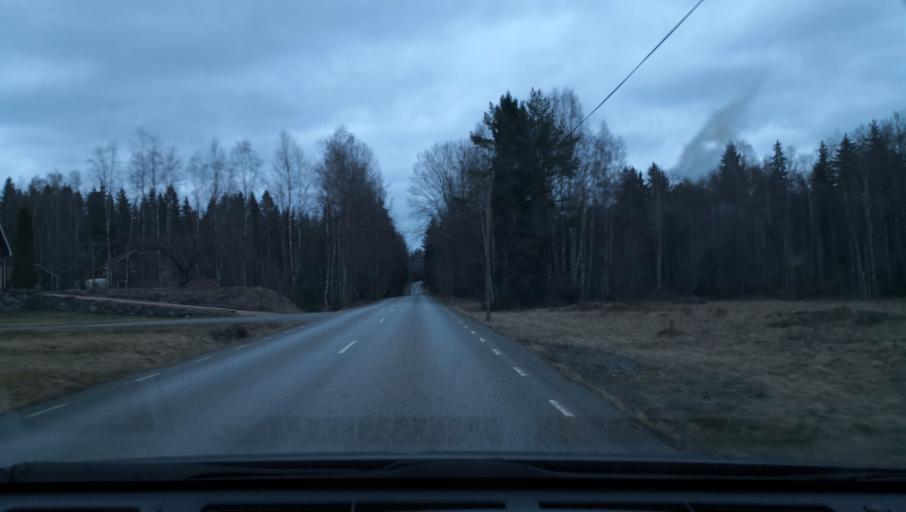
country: SE
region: Vaestmanland
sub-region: Kopings Kommun
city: Kolsva
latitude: 59.5878
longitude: 15.8081
